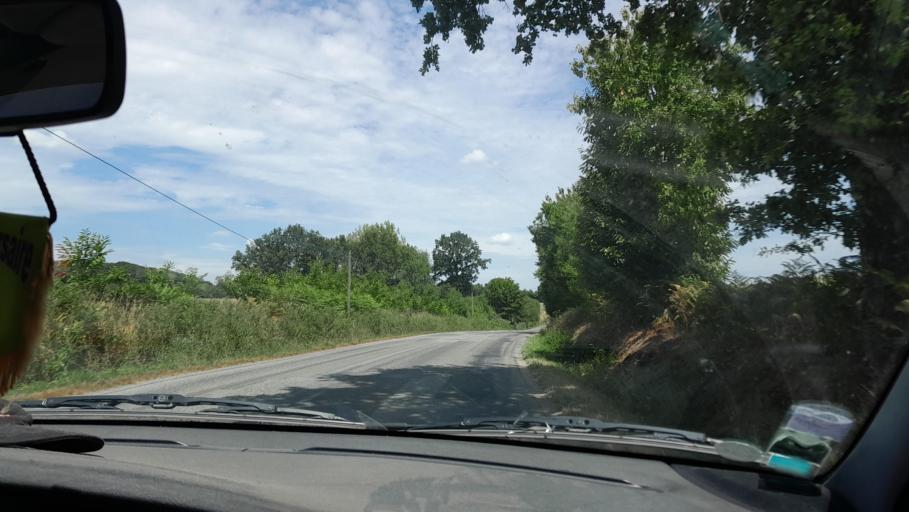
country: FR
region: Brittany
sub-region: Departement d'Ille-et-Vilaine
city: Le Pertre
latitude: 48.0508
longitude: -1.0344
